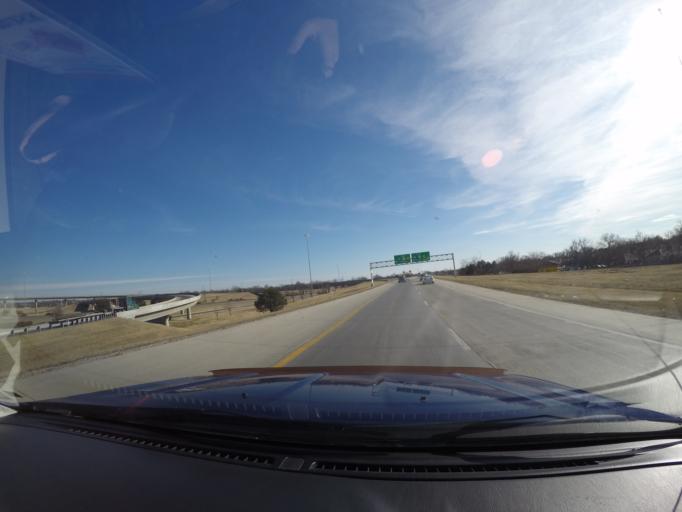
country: US
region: Kansas
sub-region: Sedgwick County
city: Wichita
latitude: 37.6777
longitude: -97.3149
